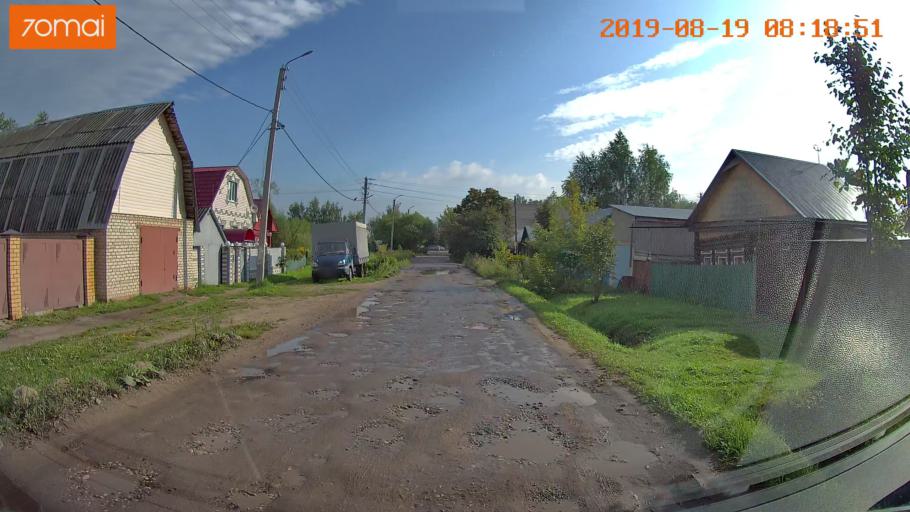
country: RU
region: Ivanovo
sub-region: Gorod Ivanovo
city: Ivanovo
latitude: 56.9772
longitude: 41.0024
